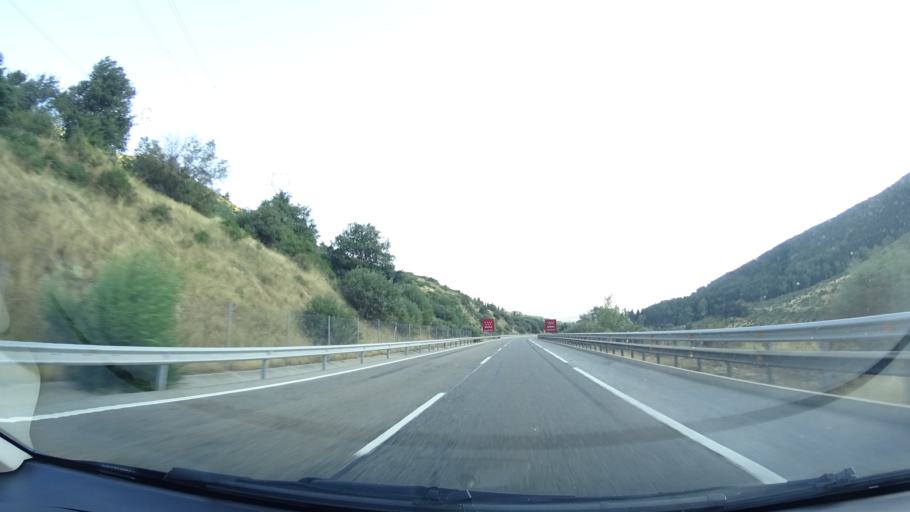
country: ES
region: Madrid
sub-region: Provincia de Madrid
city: Somosierra
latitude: 41.1571
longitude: -3.5844
